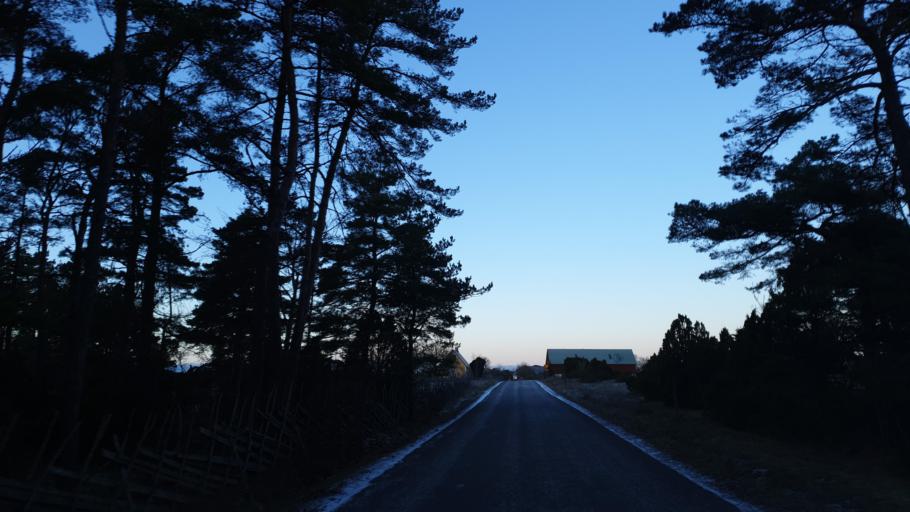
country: SE
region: Gotland
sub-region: Gotland
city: Slite
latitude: 57.3930
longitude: 18.8081
